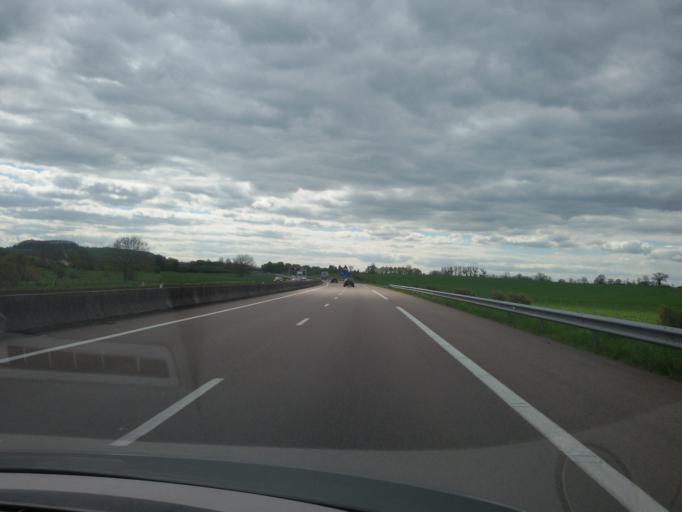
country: FR
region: Bourgogne
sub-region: Departement de la Cote-d'Or
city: Pouilly-en-Auxois
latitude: 47.2693
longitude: 4.5140
